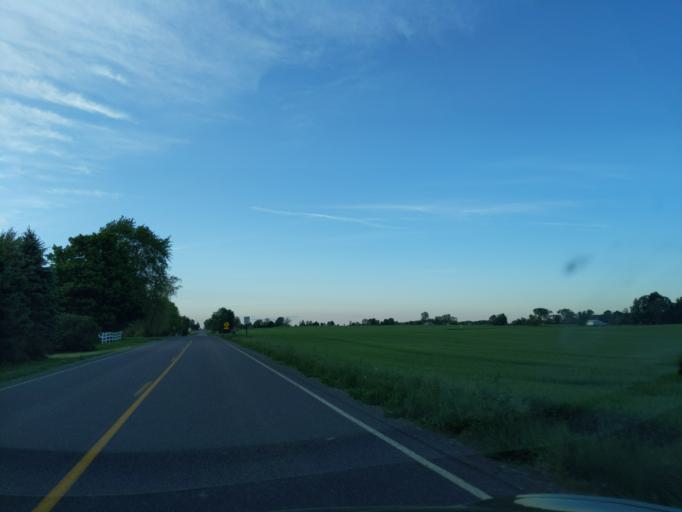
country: US
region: Michigan
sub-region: Ingham County
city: Williamston
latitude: 42.5745
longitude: -84.2984
